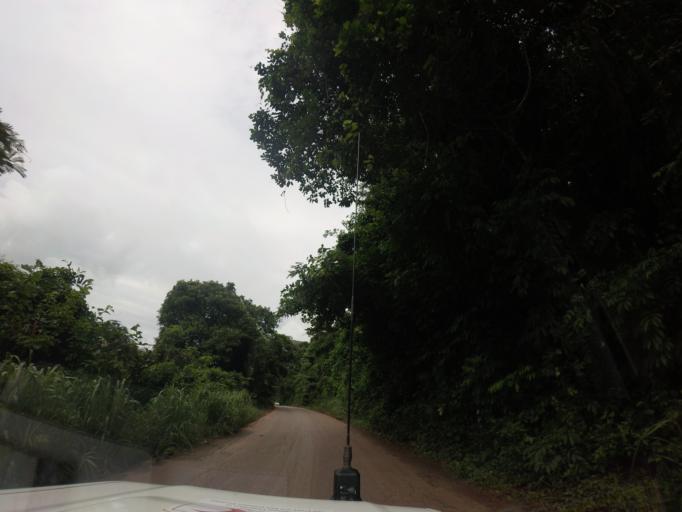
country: GN
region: Kindia
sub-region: Coyah
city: Coyah
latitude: 9.7399
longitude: -13.3698
